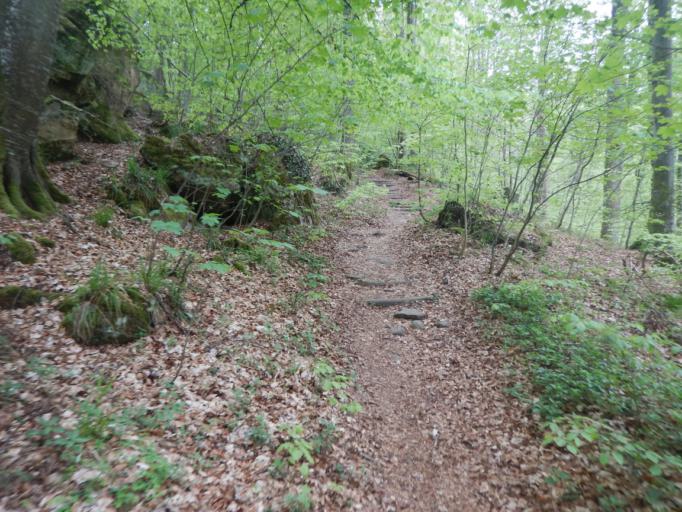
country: LU
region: Grevenmacher
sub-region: Canton d'Echternach
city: Berdorf
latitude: 49.8076
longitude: 6.3276
